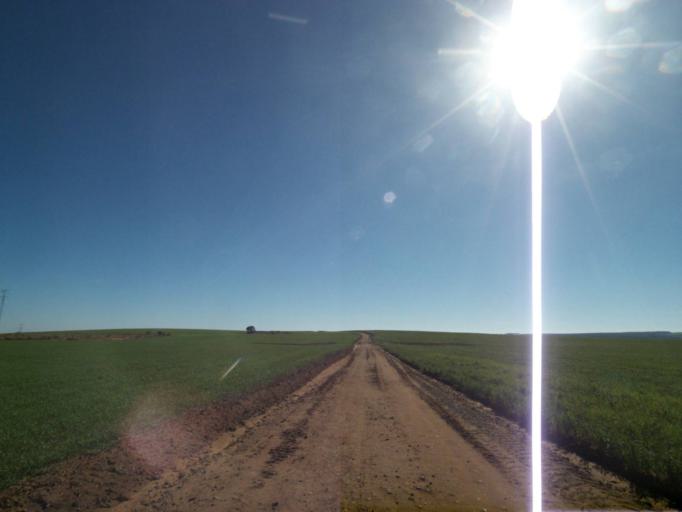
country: BR
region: Parana
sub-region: Tibagi
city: Tibagi
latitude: -24.5773
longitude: -50.2656
